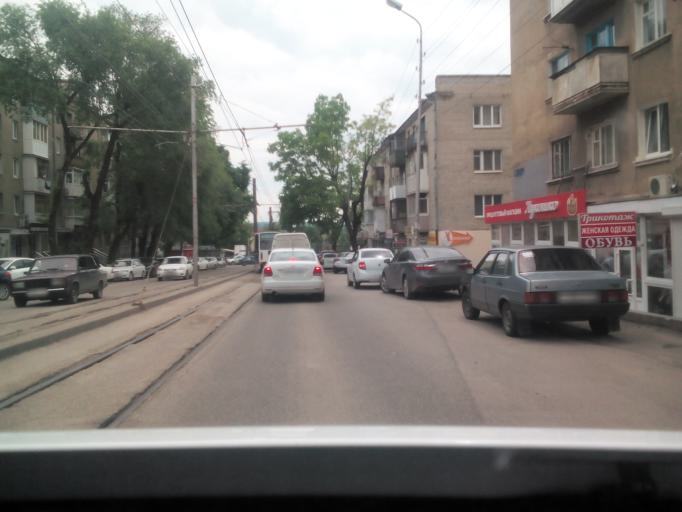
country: RU
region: Stavropol'skiy
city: Pyatigorsk
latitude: 44.0467
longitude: 43.0636
